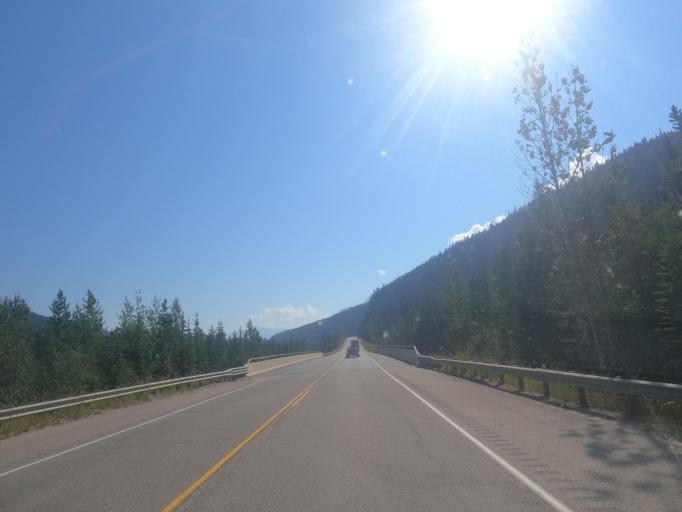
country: CA
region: Alberta
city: Jasper Park Lodge
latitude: 52.8757
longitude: -118.3156
